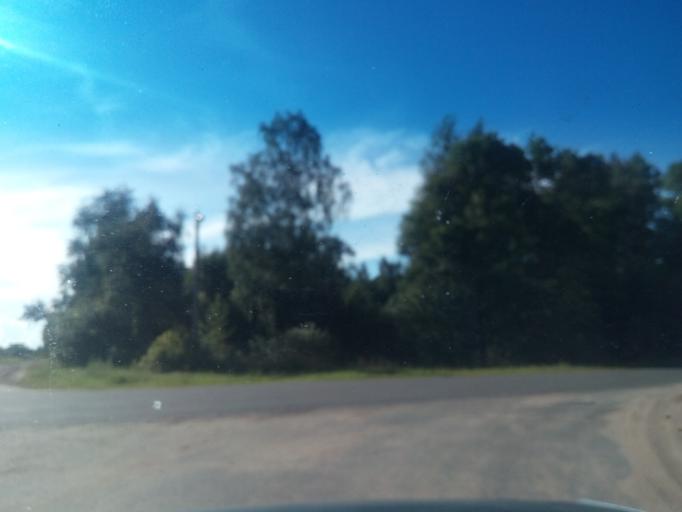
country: BY
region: Vitebsk
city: Dzisna
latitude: 55.6544
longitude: 28.3225
